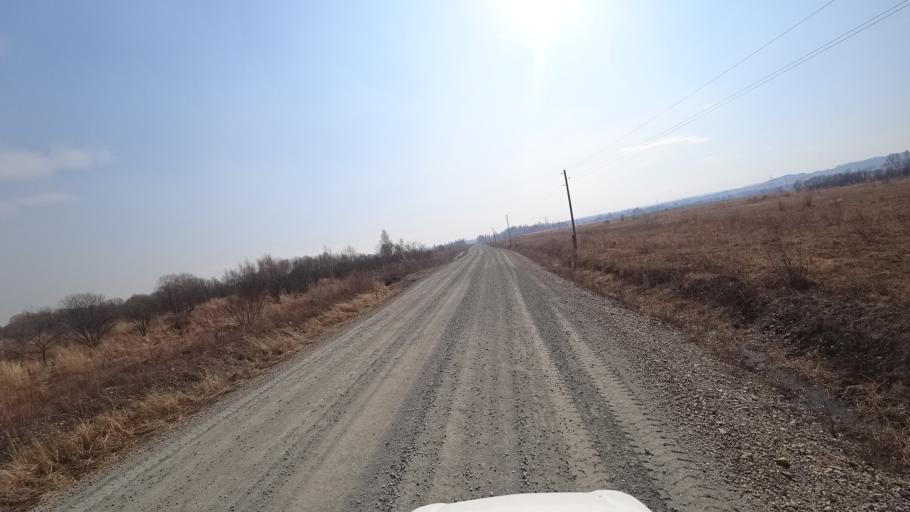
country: RU
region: Amur
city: Novobureyskiy
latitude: 49.8097
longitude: 129.9681
